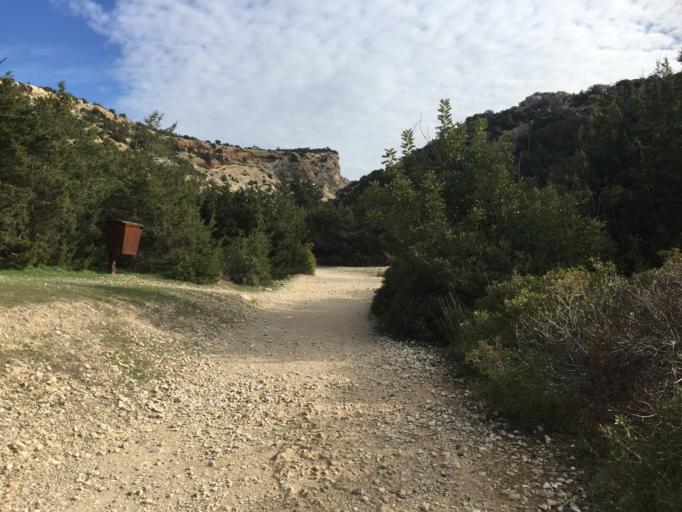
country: CY
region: Pafos
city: Pegeia
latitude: 34.9222
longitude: 32.3396
